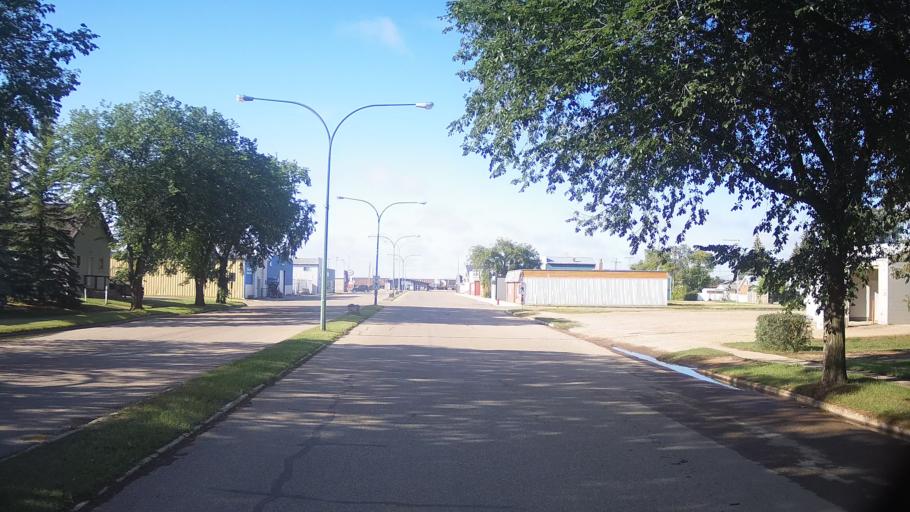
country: CA
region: Saskatchewan
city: Lanigan
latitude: 51.8477
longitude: -105.0328
